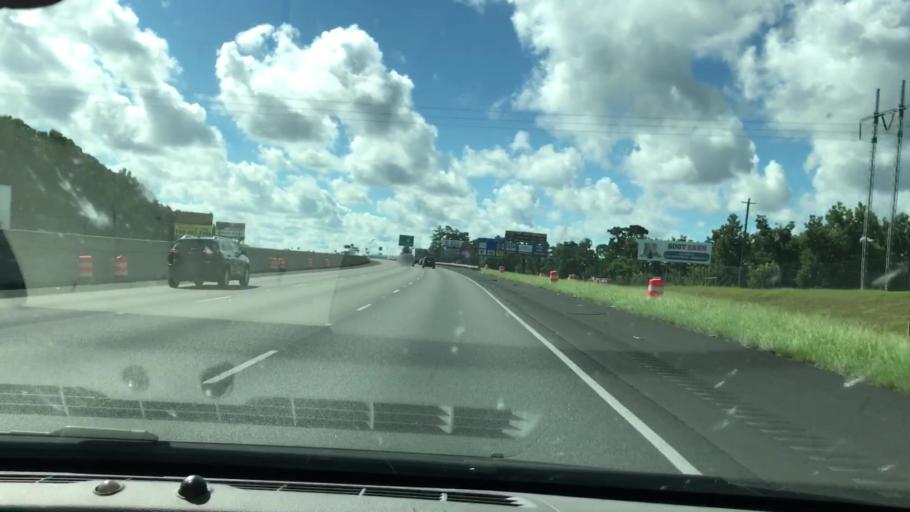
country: US
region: Georgia
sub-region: Lowndes County
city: Remerton
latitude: 30.9028
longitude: -83.3616
